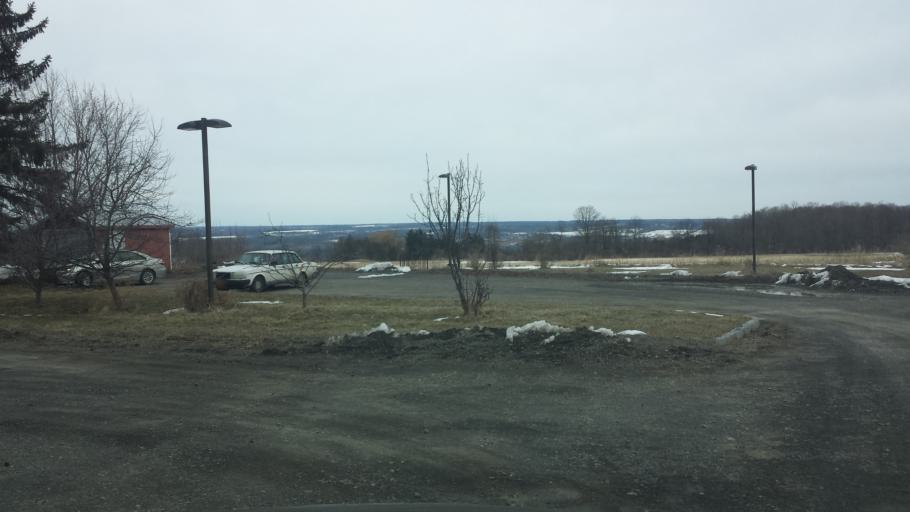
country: US
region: New York
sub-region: Tompkins County
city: Northwest Ithaca
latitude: 42.4935
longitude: -76.5738
